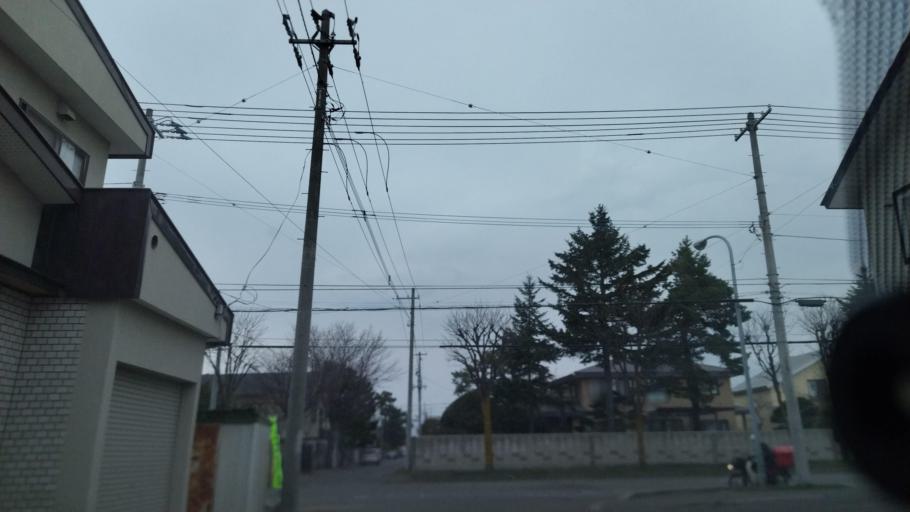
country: JP
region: Hokkaido
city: Obihiro
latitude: 42.9223
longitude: 143.2200
